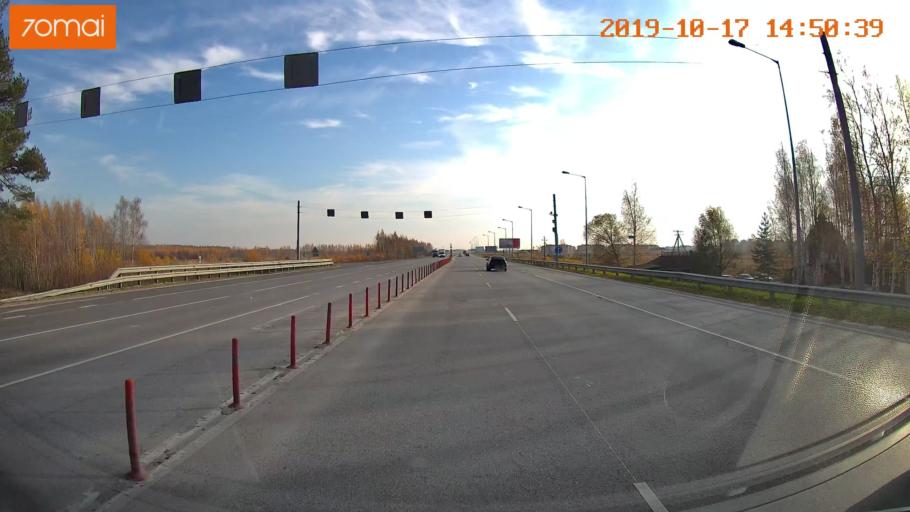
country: RU
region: Rjazan
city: Polyany
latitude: 54.7309
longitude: 39.8437
